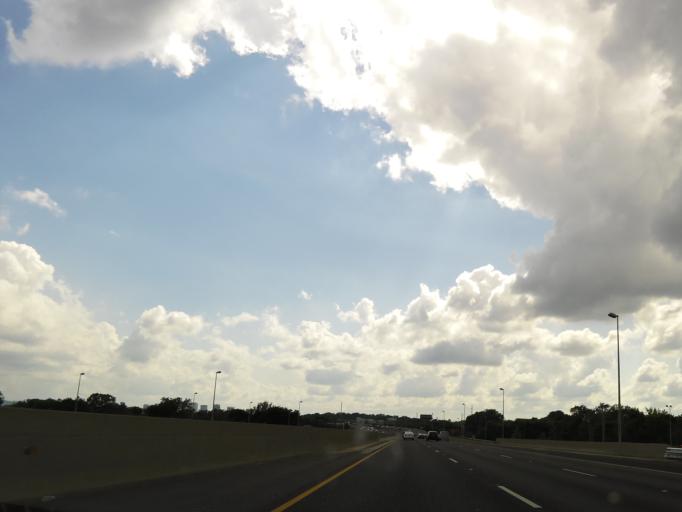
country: US
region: Alabama
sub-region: Jefferson County
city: Tarrant
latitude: 33.5483
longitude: -86.7794
